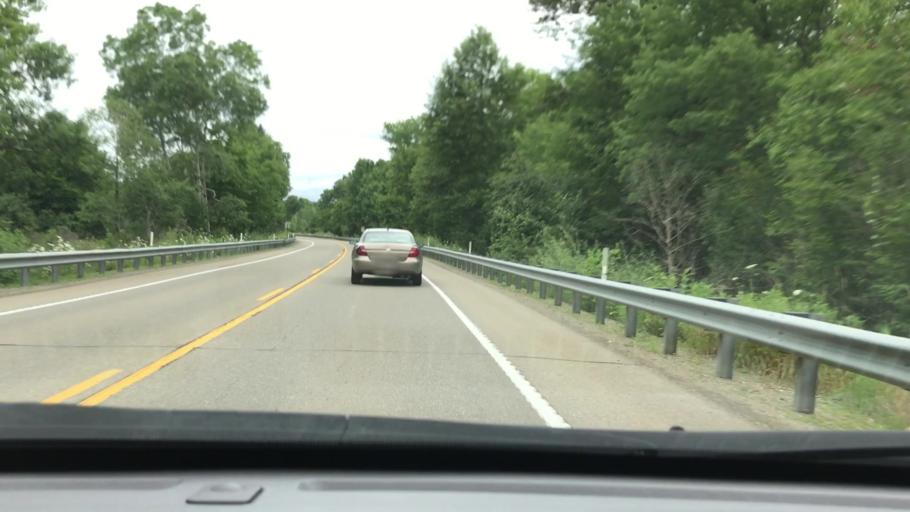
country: US
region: Pennsylvania
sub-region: Elk County
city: Johnsonburg
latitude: 41.5112
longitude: -78.6788
